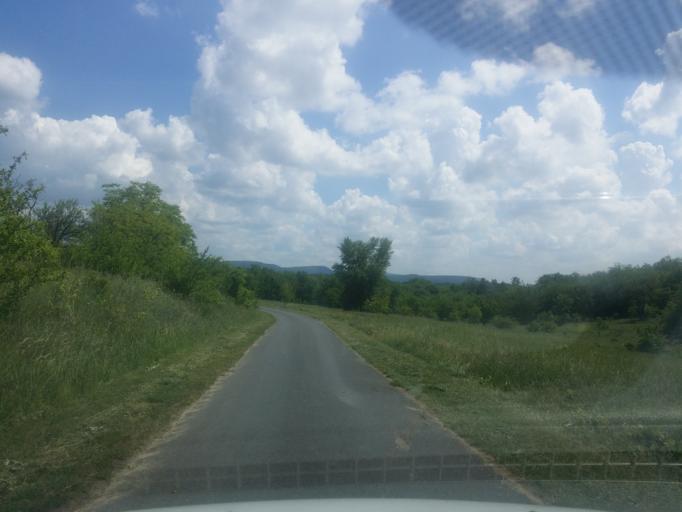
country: HU
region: Komarom-Esztergom
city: Kesztolc
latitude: 47.7196
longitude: 18.7932
